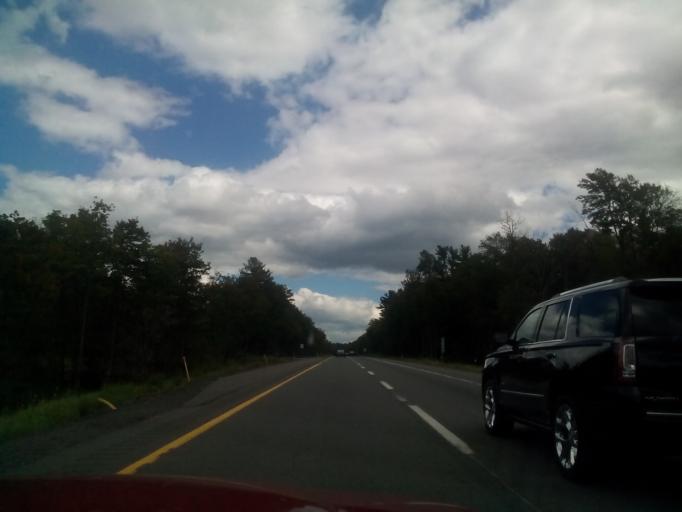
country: US
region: Pennsylvania
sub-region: Carbon County
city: Towamensing Trails
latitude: 41.0763
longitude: -75.5689
